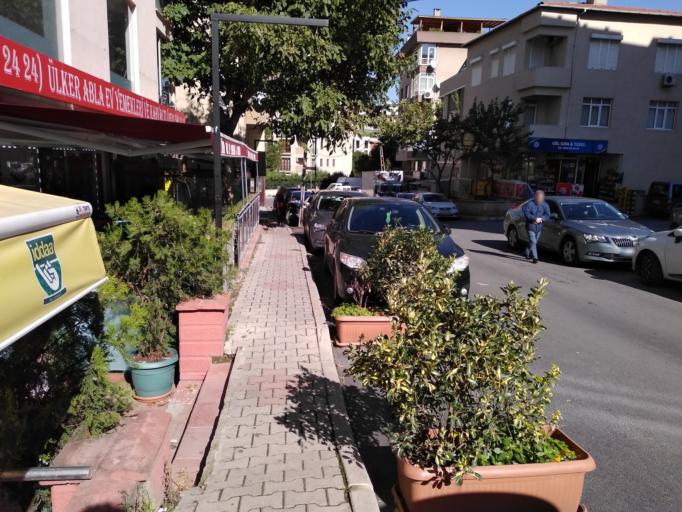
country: TR
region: Istanbul
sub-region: Atasehir
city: Atasehir
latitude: 40.9787
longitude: 29.1199
